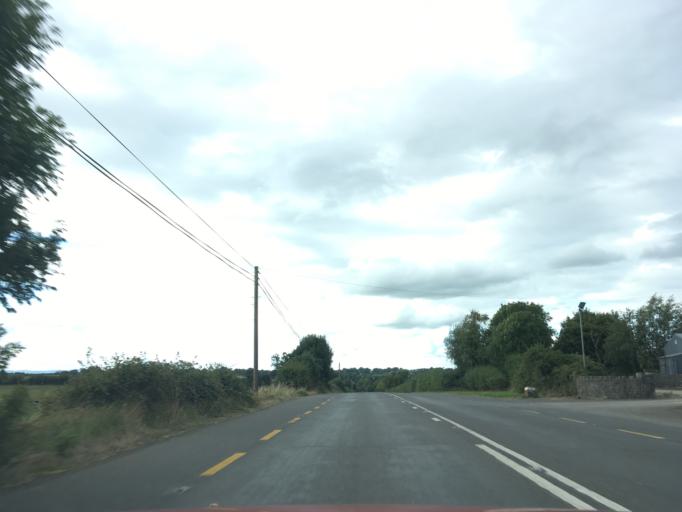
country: IE
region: Munster
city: Cahir
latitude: 52.4190
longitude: -7.8885
